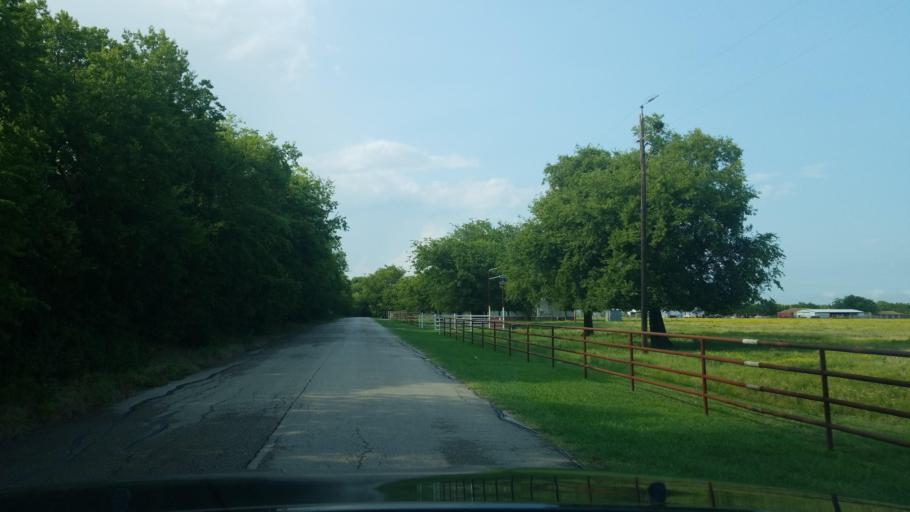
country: US
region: Texas
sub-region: Denton County
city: Cross Roads
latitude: 33.2517
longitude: -97.0614
